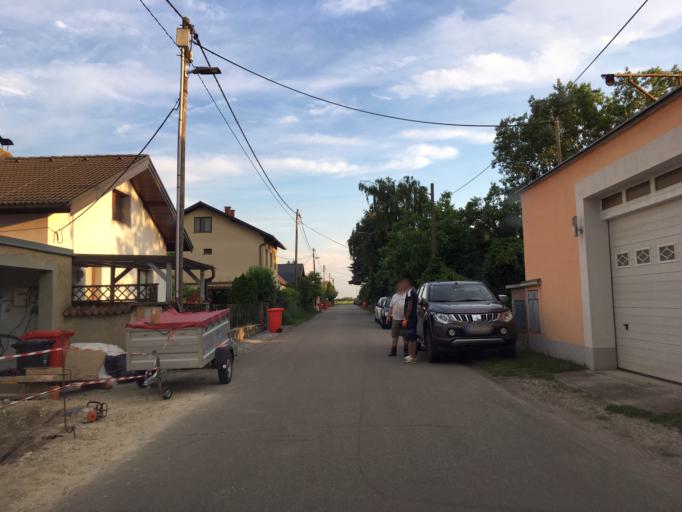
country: AT
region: Lower Austria
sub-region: Politischer Bezirk Wien-Umgebung
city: Gerasdorf bei Wien
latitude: 48.3126
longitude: 16.4950
